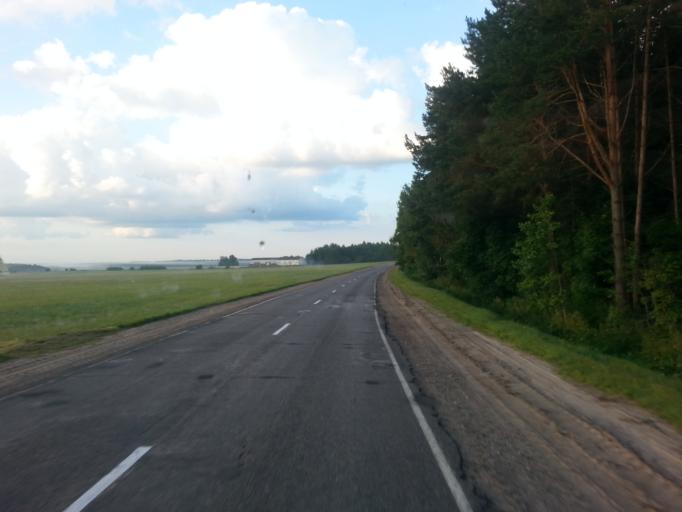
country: BY
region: Minsk
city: Il'ya
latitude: 54.5588
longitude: 27.2130
